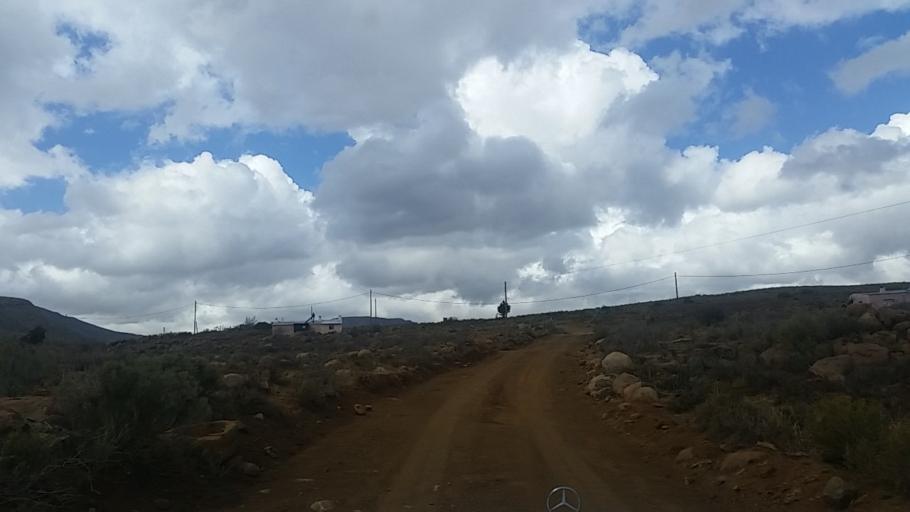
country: ZA
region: Eastern Cape
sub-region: Chris Hani District Municipality
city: Middelburg
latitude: -31.7918
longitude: 24.6596
